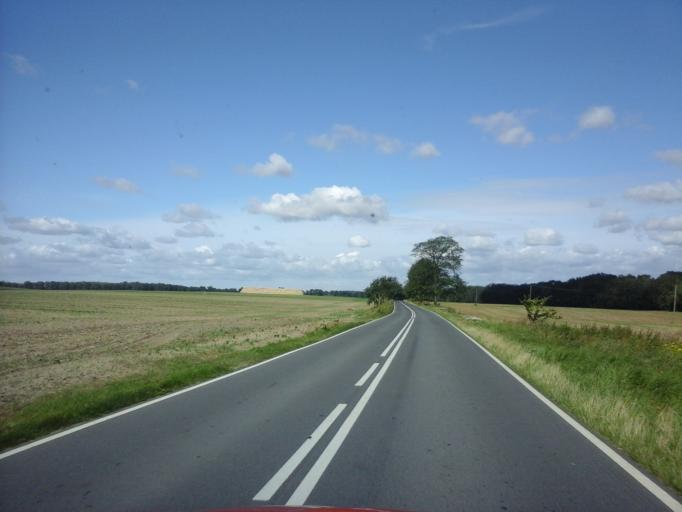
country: PL
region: West Pomeranian Voivodeship
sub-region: Powiat stargardzki
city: Dolice
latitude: 53.1996
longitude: 15.1690
